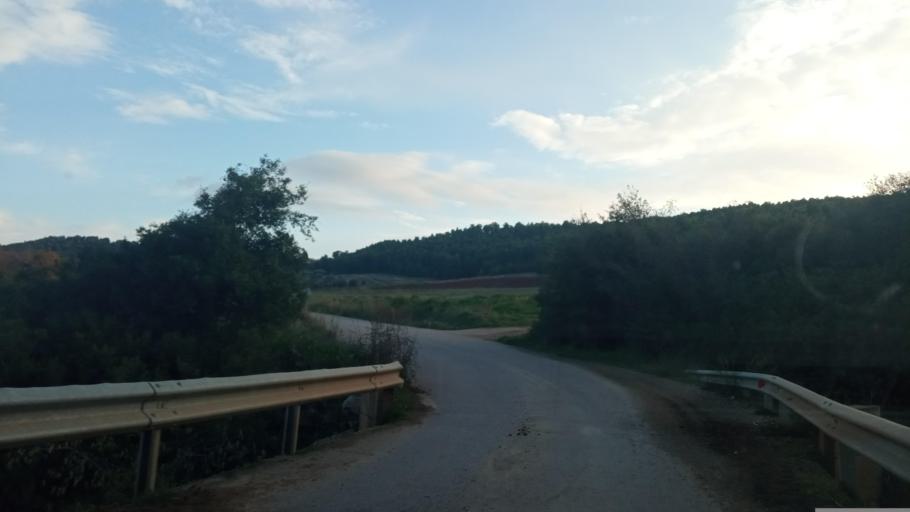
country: GR
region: Central Greece
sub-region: Nomos Evvoias
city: Kastella
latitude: 38.5526
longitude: 23.7142
